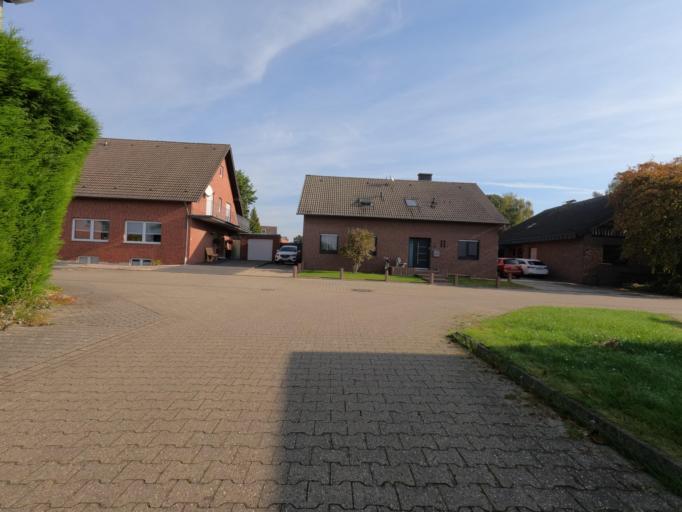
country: DE
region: North Rhine-Westphalia
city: Huckelhoven
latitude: 51.0446
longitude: 6.2404
